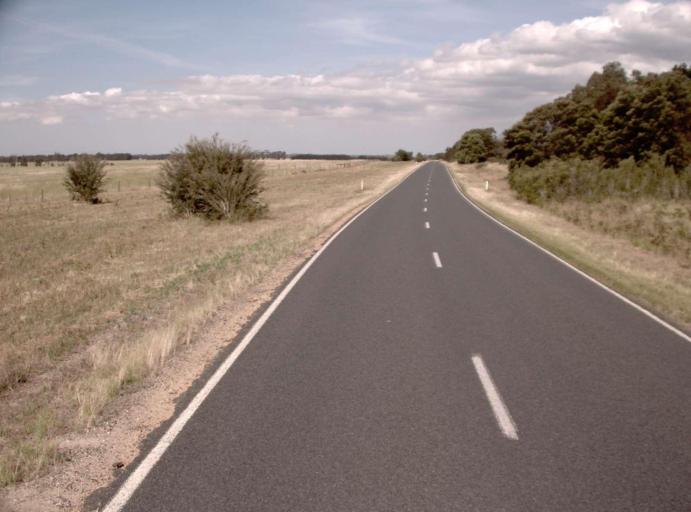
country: AU
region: Victoria
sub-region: Wellington
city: Heyfield
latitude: -38.1620
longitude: 146.8665
